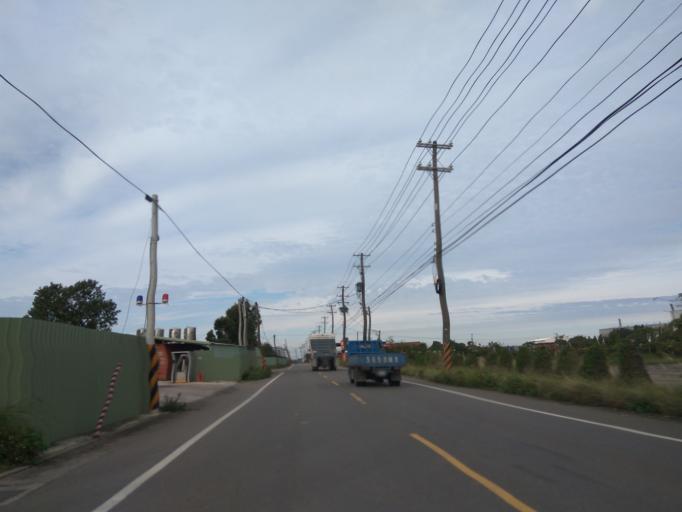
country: TW
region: Taiwan
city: Daxi
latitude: 24.9437
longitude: 121.1518
